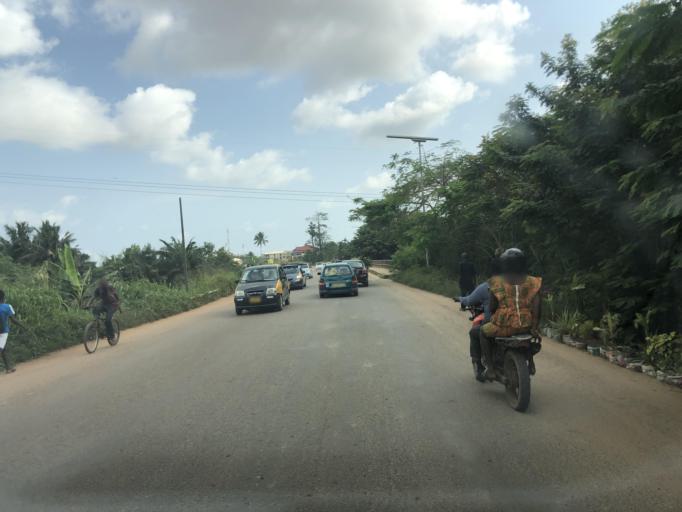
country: GH
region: Central
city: Cape Coast
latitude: 5.1480
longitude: -1.2878
